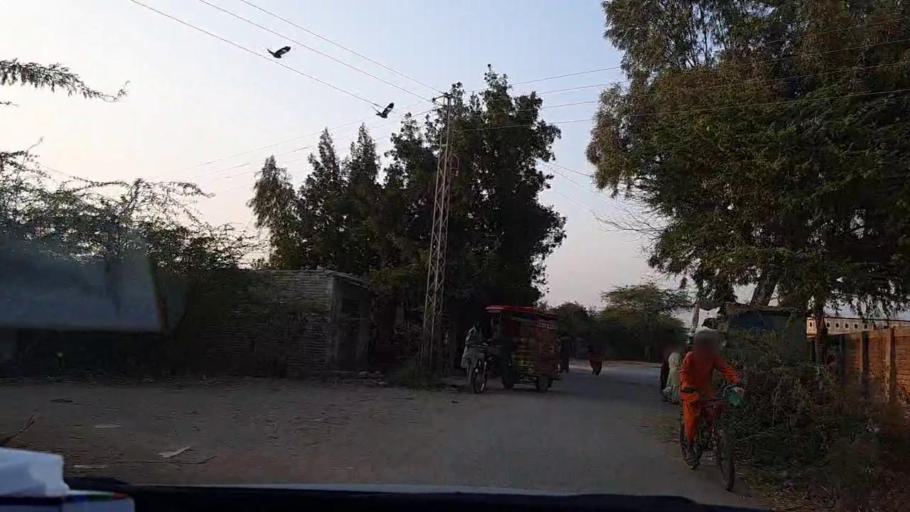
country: PK
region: Sindh
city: Tando Ghulam Ali
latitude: 25.1722
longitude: 68.9361
